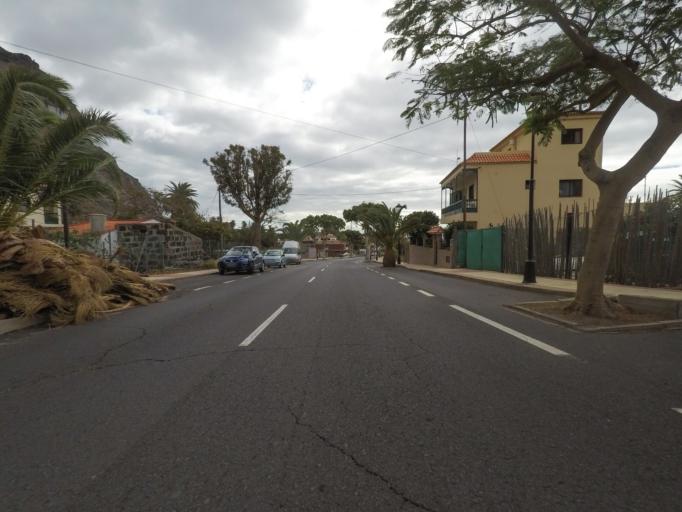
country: ES
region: Canary Islands
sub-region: Provincia de Santa Cruz de Tenerife
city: Alajero
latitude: 28.0927
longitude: -17.3353
